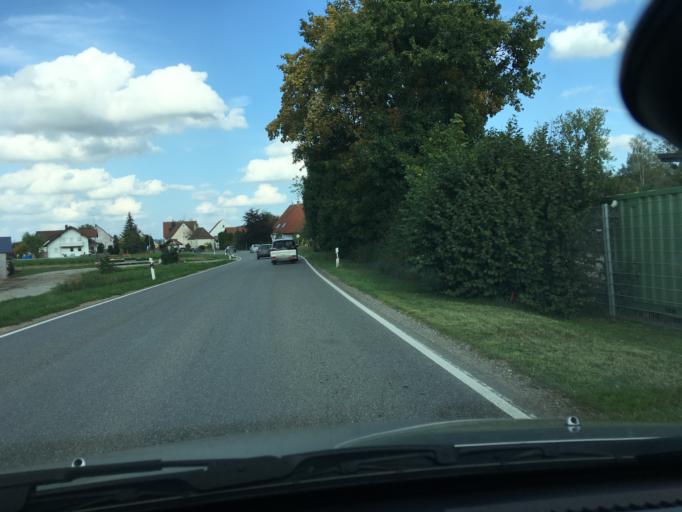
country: DE
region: Baden-Wuerttemberg
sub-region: Tuebingen Region
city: Hochdorf
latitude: 48.0419
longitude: 9.7963
